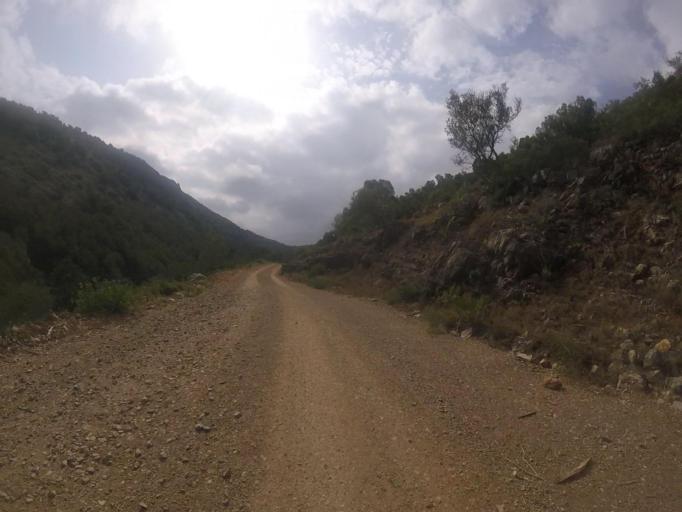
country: ES
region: Valencia
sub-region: Provincia de Castello
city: Santa Magdalena de Pulpis
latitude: 40.3485
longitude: 0.3116
